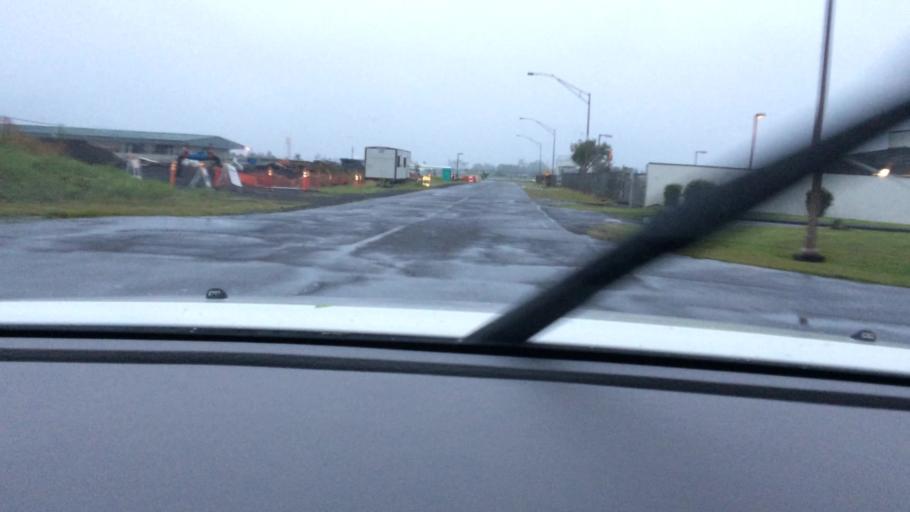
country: US
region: Hawaii
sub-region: Hawaii County
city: Hilo
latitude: 19.7156
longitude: -155.0509
